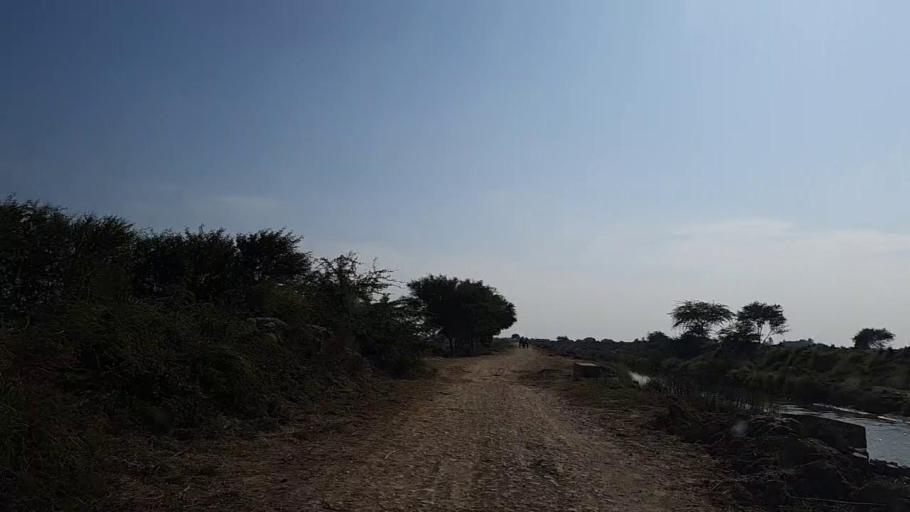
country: PK
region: Sindh
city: Daro Mehar
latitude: 24.7292
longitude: 68.1160
